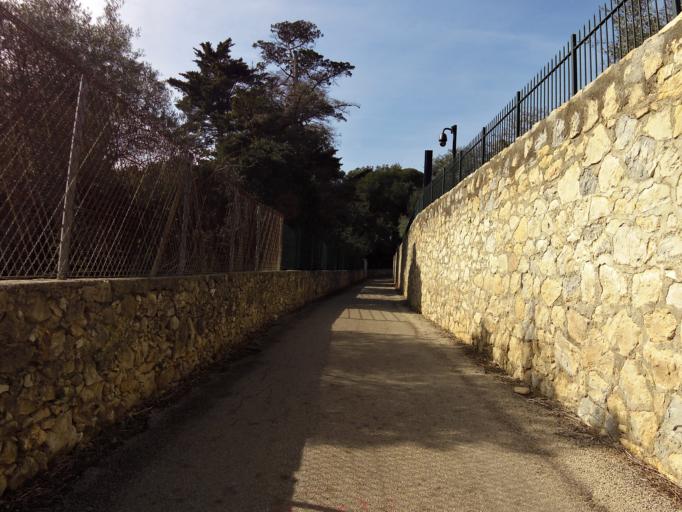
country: FR
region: Provence-Alpes-Cote d'Azur
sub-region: Departement des Alpes-Maritimes
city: Antibes
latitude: 43.5474
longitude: 7.1321
